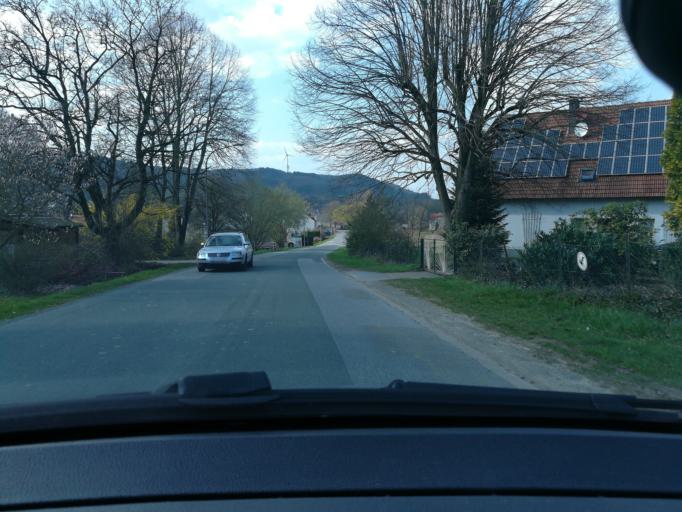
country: DE
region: North Rhine-Westphalia
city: Borgholzhausen
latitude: 52.1049
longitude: 8.3112
